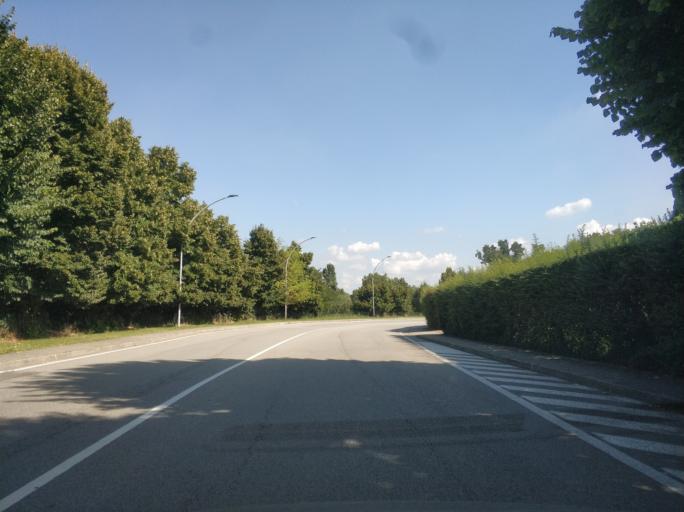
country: IT
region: Piedmont
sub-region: Provincia di Torino
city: Rivarolo Canavese
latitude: 45.3330
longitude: 7.7282
